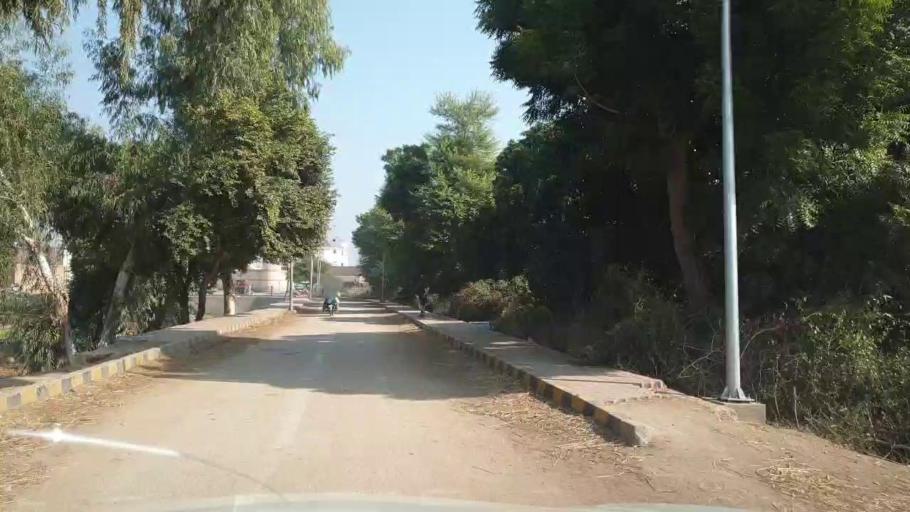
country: PK
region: Sindh
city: Bhan
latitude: 26.5404
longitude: 67.7773
